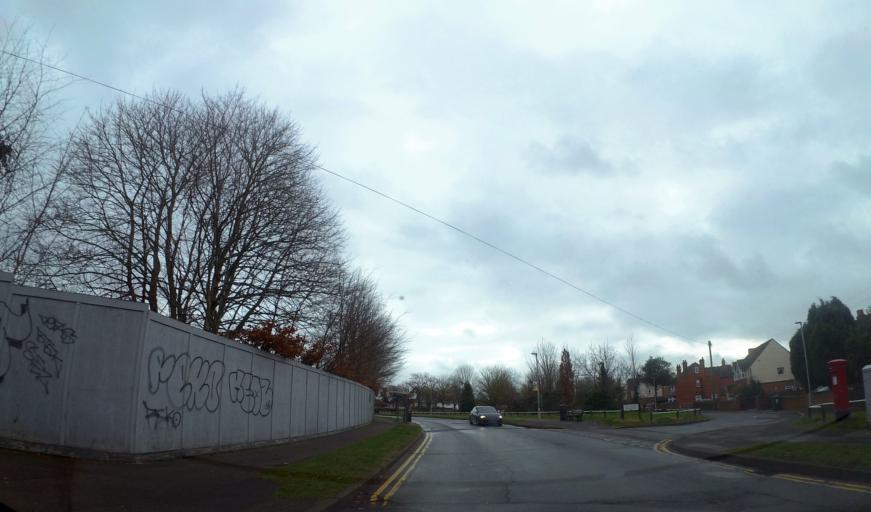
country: GB
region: England
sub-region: West Berkshire
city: Tilehurst
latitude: 51.4416
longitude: -1.0204
